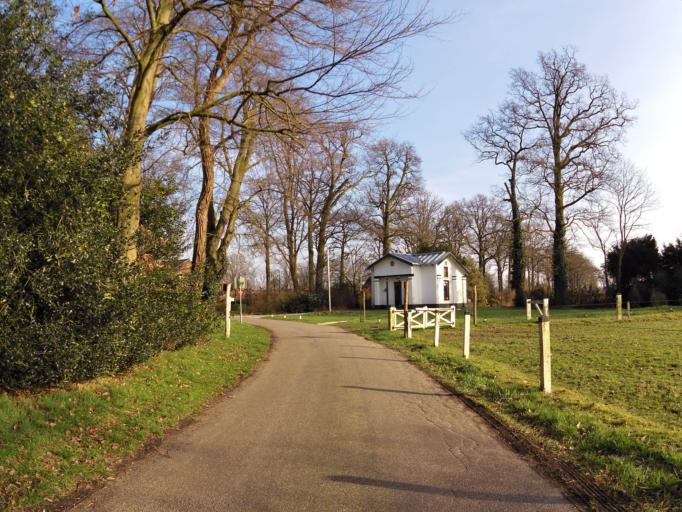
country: NL
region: North Brabant
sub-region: Gemeente Haaren
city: Haaren
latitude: 51.6429
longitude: 5.2244
